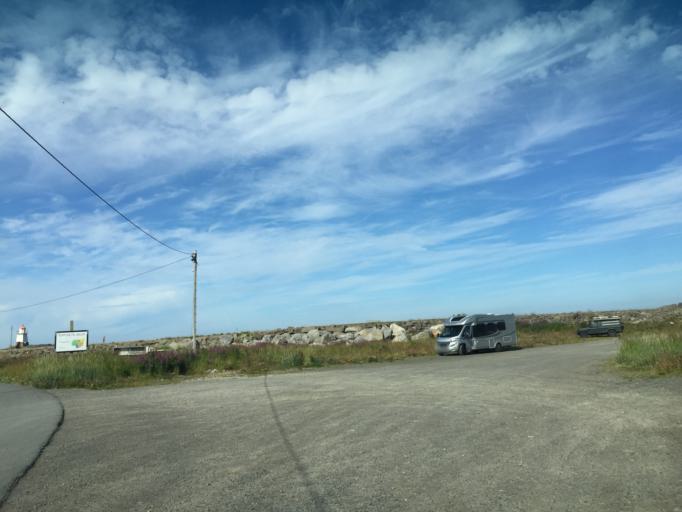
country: NO
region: Nordland
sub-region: Vagan
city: Kabelvag
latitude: 68.3896
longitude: 14.4134
